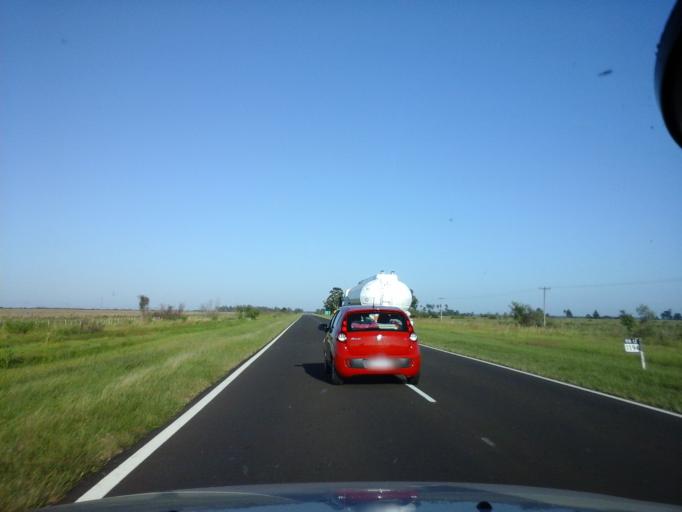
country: AR
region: Corrientes
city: Ita Ibate
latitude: -27.4978
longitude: -57.2594
